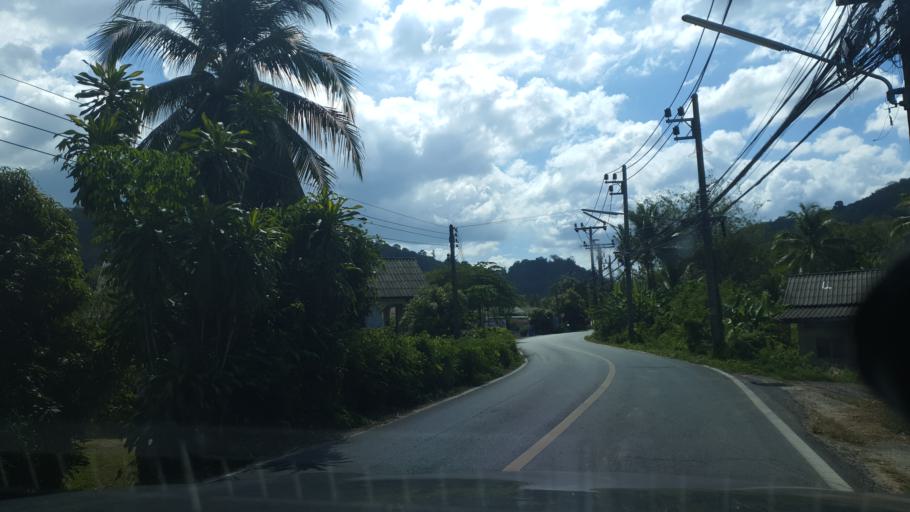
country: TH
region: Phuket
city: Thalang
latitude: 8.0715
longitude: 98.2964
